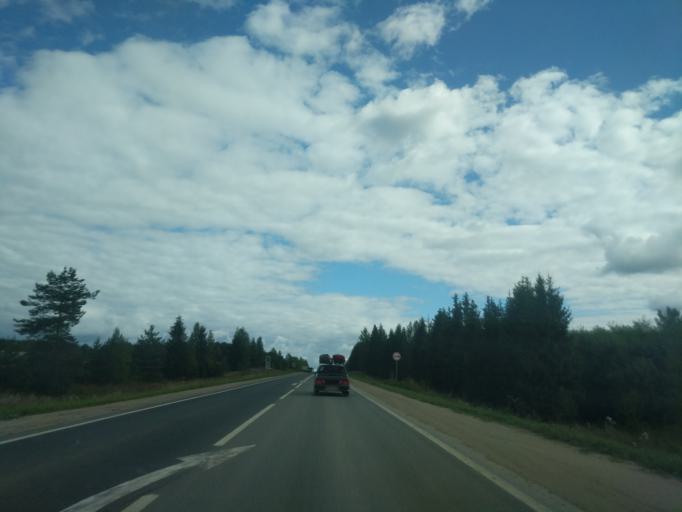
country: RU
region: Kostroma
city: Sudislavl'
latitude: 57.8720
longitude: 41.7421
